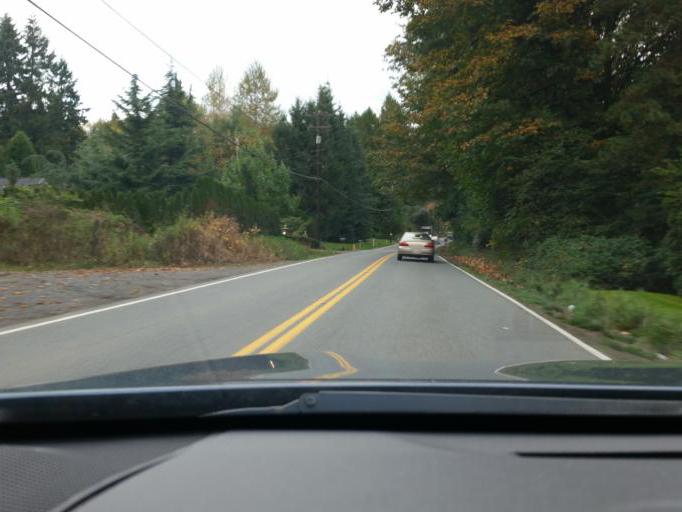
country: US
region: Washington
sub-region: Snohomish County
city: Maltby
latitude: 47.8050
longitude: -122.1334
